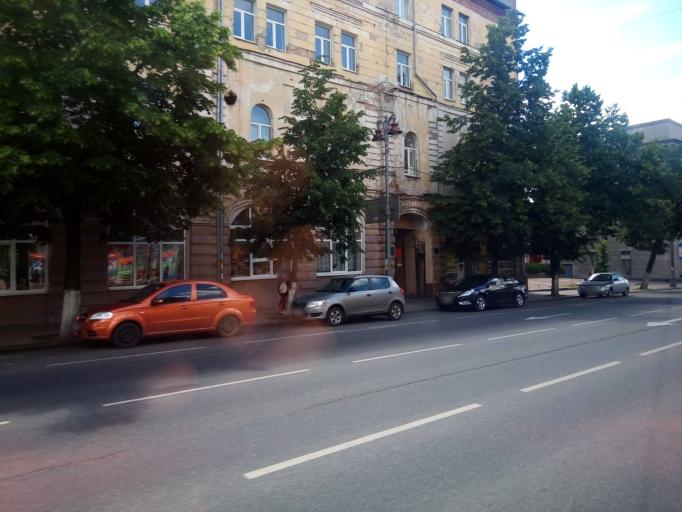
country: RU
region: Kursk
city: Kursk
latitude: 51.7343
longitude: 36.1932
